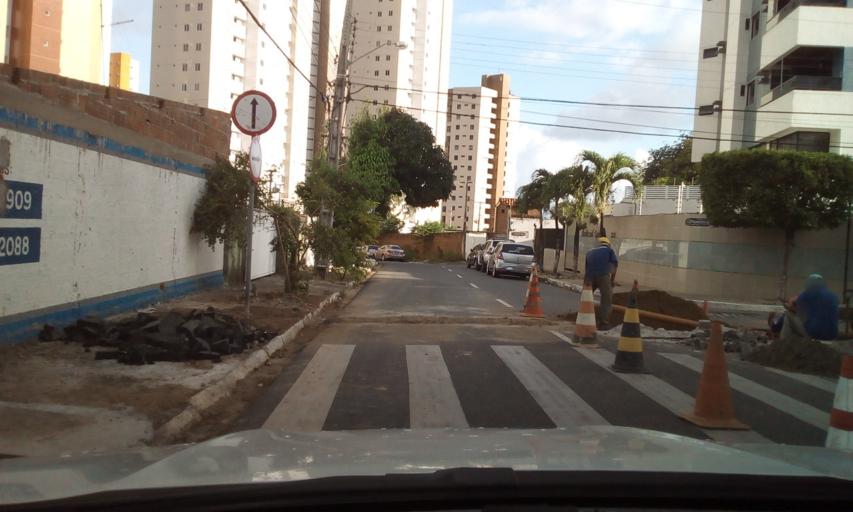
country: BR
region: Paraiba
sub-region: Joao Pessoa
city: Joao Pessoa
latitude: -7.1224
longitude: -34.8330
